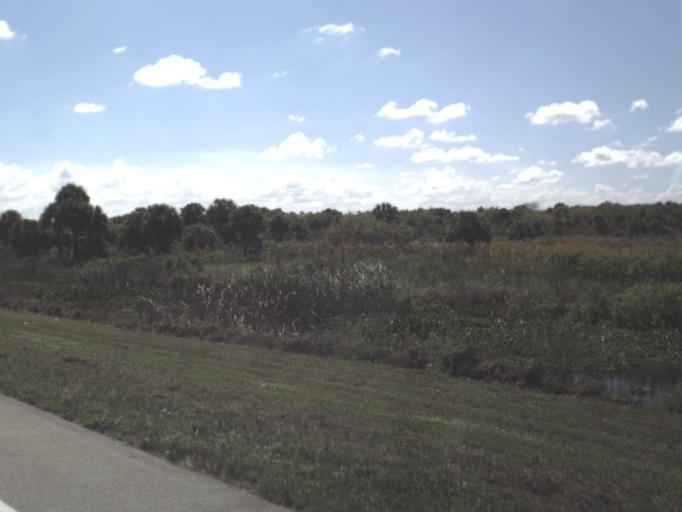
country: US
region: Florida
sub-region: Glades County
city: Moore Haven
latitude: 26.9316
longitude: -81.1223
